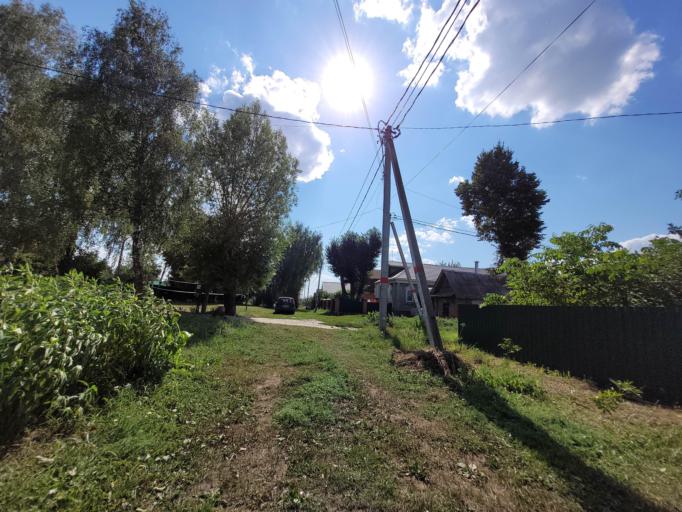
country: RU
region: Moskovskaya
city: Peski
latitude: 55.2309
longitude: 38.7478
